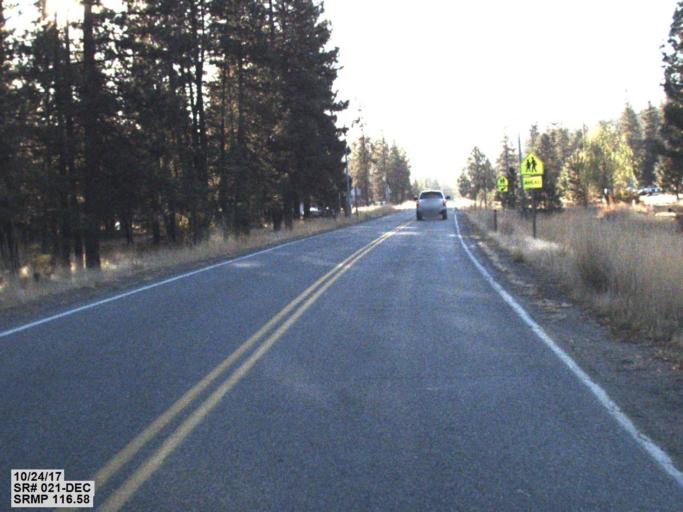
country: US
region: Washington
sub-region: Okanogan County
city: Coulee Dam
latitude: 48.0773
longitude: -118.6825
